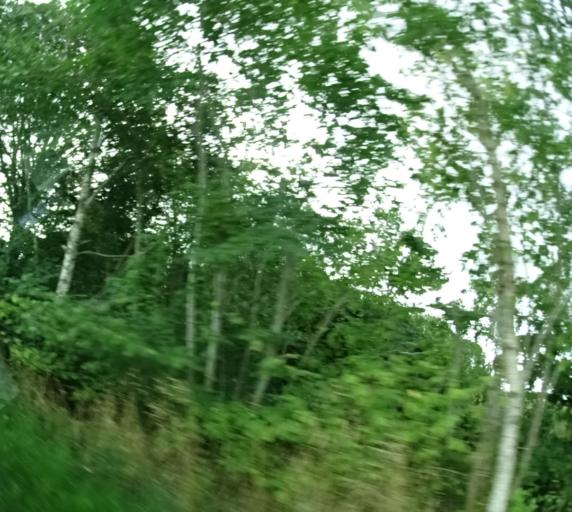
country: DK
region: Central Jutland
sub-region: Syddjurs Kommune
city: Ryomgard
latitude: 56.3887
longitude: 10.5552
